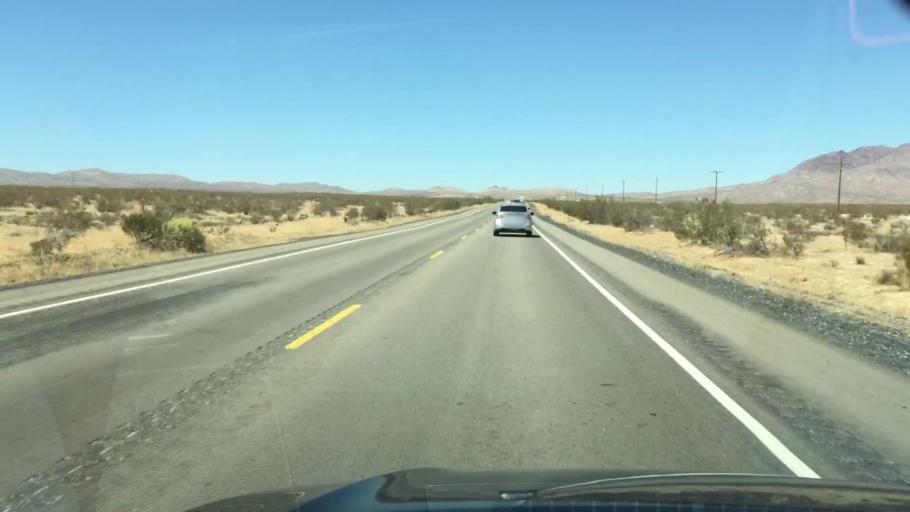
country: US
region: California
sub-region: Kern County
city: Boron
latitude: 35.2675
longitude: -117.6139
